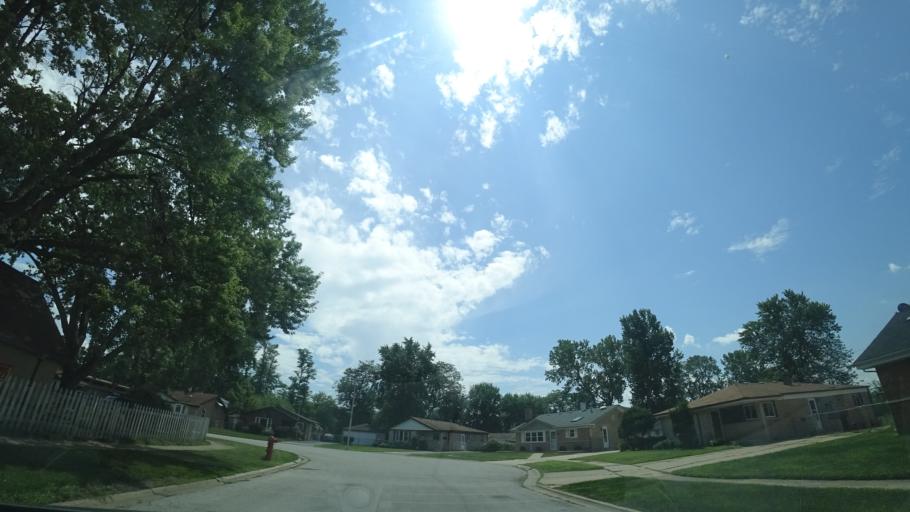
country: US
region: Illinois
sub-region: Cook County
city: Alsip
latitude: 41.6662
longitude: -87.7334
